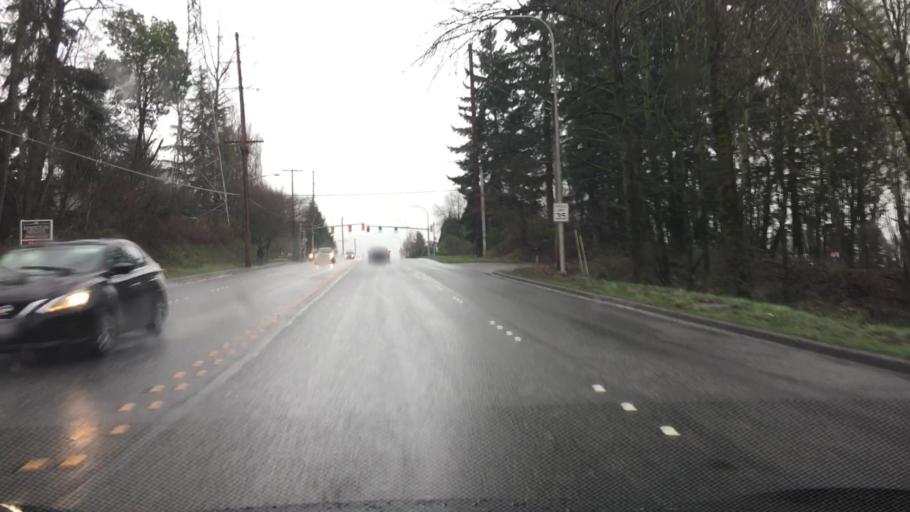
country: US
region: Washington
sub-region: King County
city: Renton
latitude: 47.4857
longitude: -122.1876
